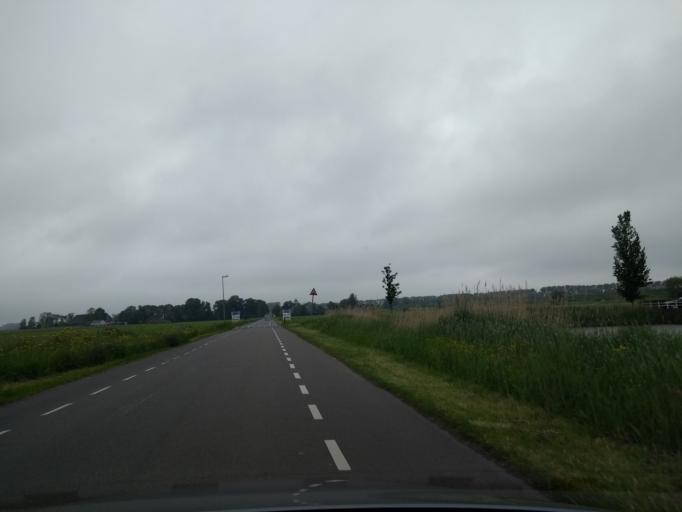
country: NL
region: Groningen
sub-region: Gemeente Groningen
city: Korrewegwijk
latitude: 53.2463
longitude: 6.5175
